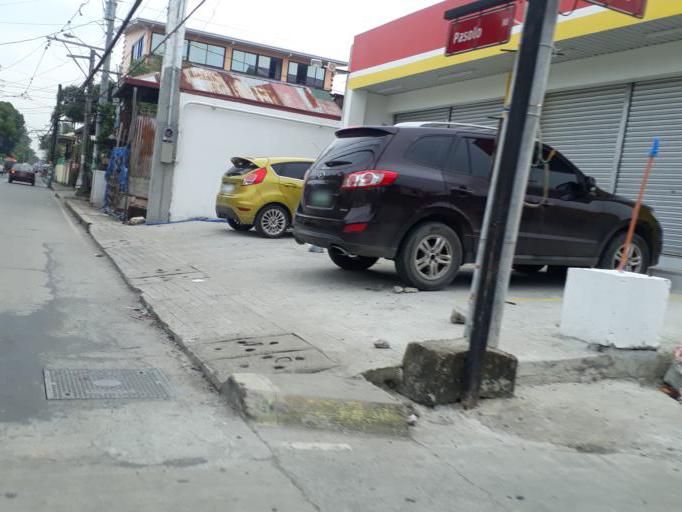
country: PH
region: Calabarzon
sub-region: Province of Rizal
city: Valenzuela
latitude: 14.7059
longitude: 120.9538
